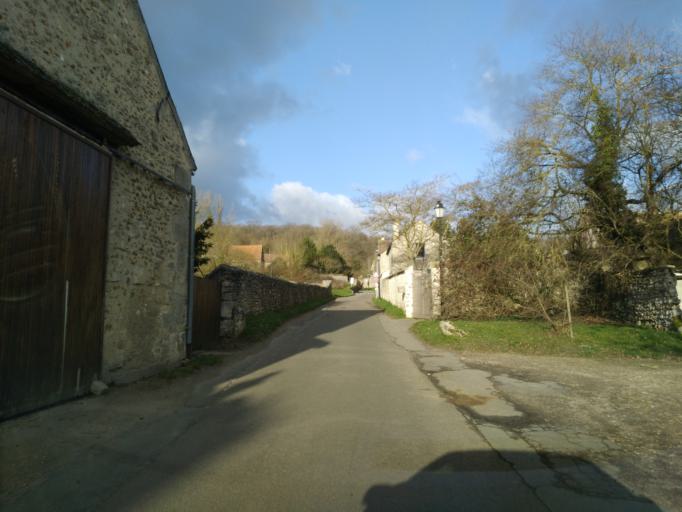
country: FR
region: Ile-de-France
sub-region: Departement des Yvelines
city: Saint-Nom-la-Breteche
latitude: 48.8702
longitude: 2.0081
